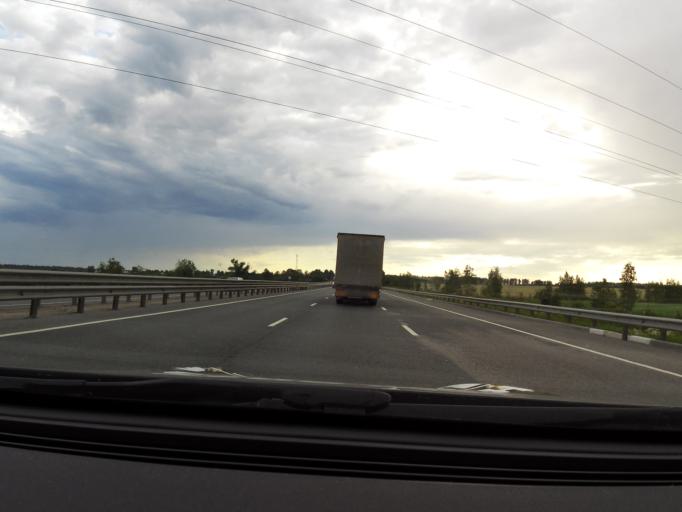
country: RU
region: Vladimir
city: Vorsha
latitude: 56.0659
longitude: 40.1427
